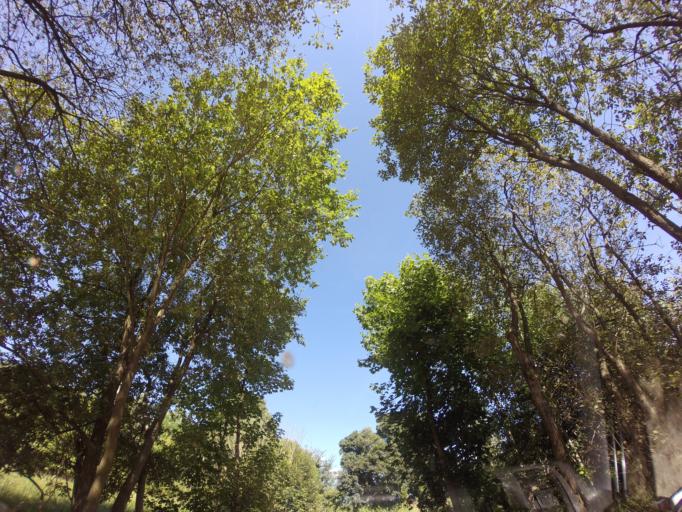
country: PL
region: West Pomeranian Voivodeship
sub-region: Powiat choszczenski
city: Recz
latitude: 53.1681
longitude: 15.5773
